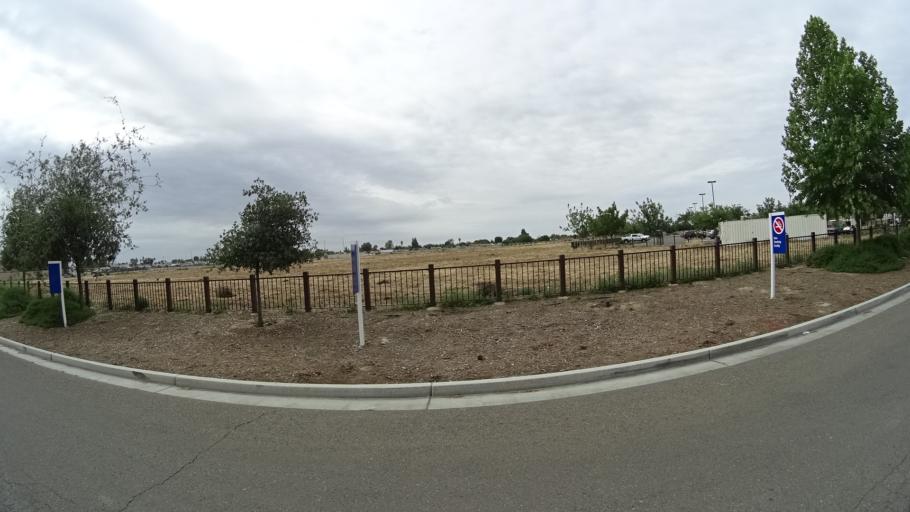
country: US
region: California
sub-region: Kings County
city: Hanford
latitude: 36.3240
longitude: -119.6652
